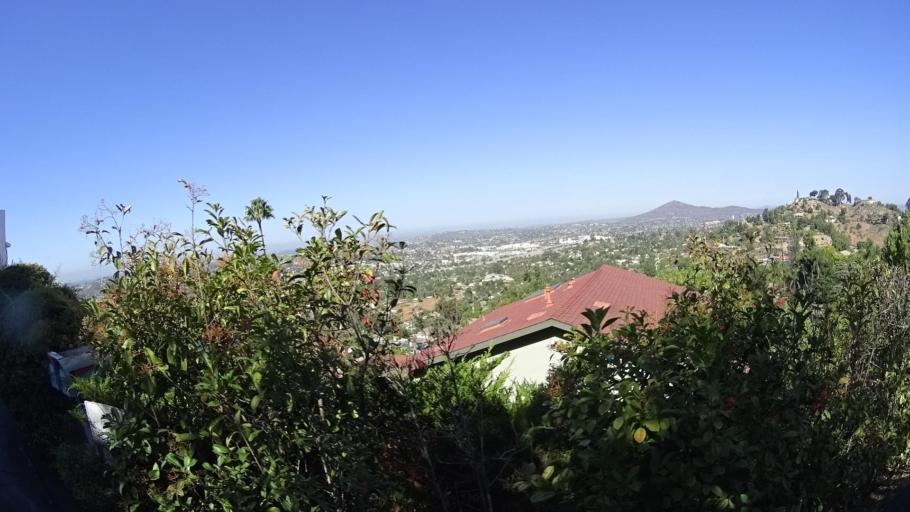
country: US
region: California
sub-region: San Diego County
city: Casa de Oro-Mount Helix
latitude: 32.7658
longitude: -116.9867
